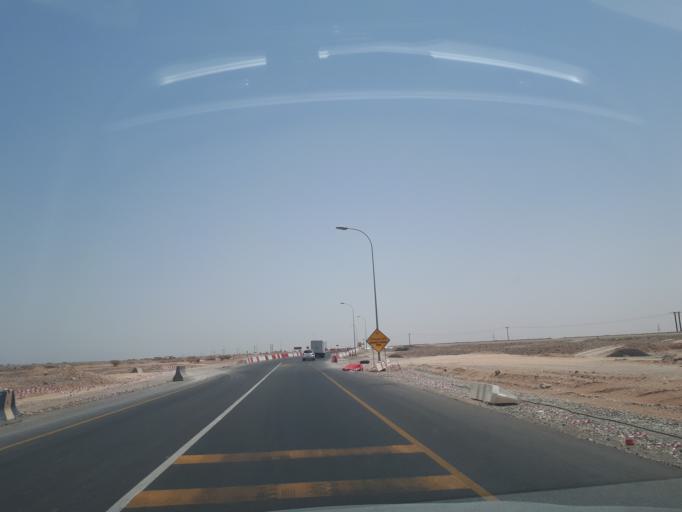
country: OM
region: Ash Sharqiyah
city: Badiyah
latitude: 22.4323
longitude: 59.0336
